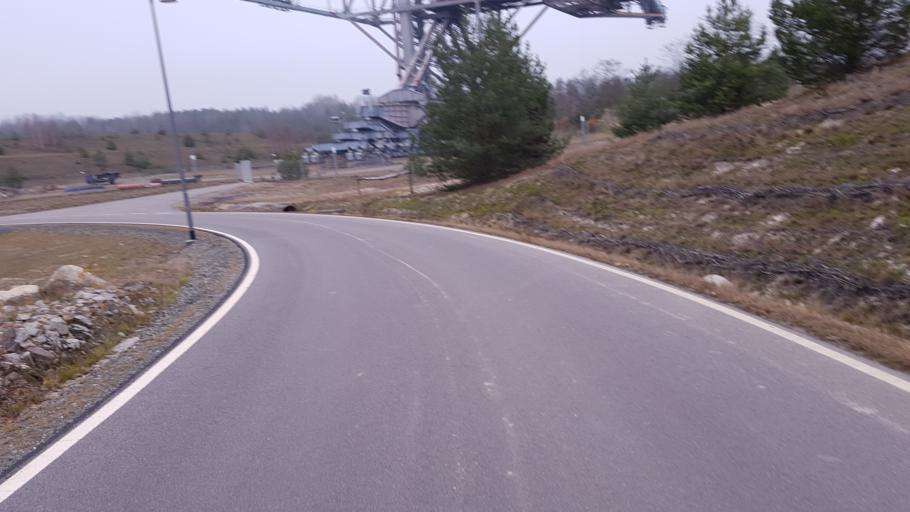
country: DE
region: Brandenburg
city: Sallgast
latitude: 51.5850
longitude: 13.7784
